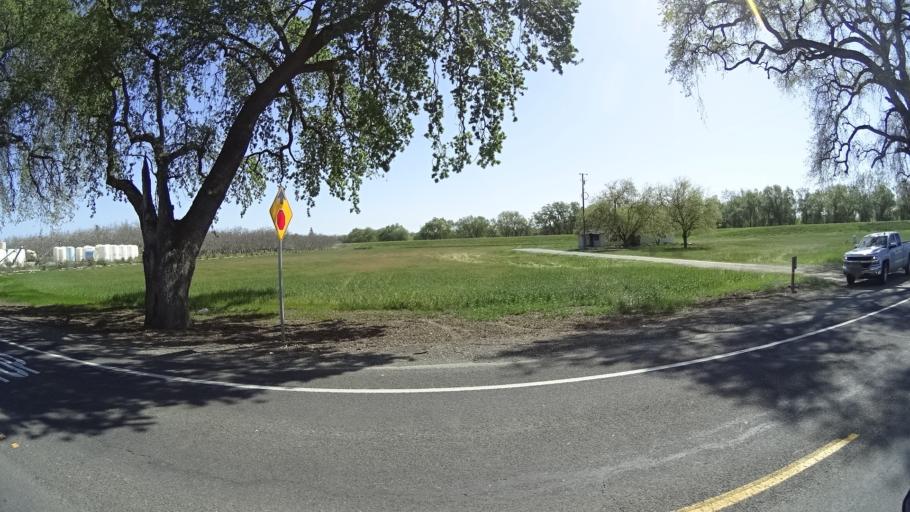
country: US
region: California
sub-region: Glenn County
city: Willows
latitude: 39.4552
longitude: -122.0172
